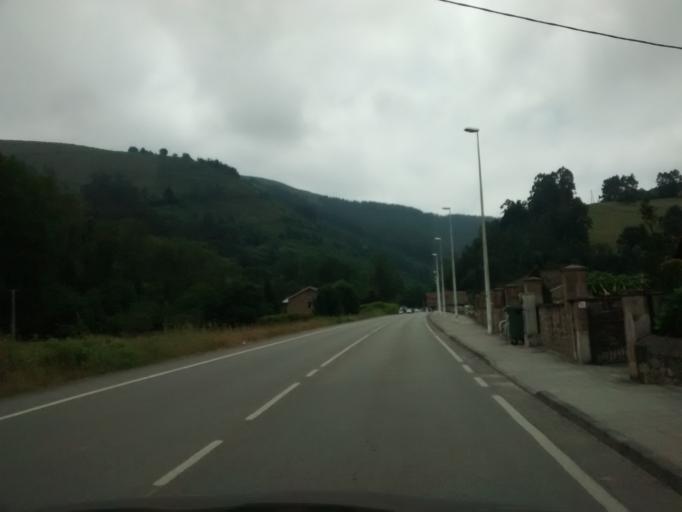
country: ES
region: Cantabria
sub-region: Provincia de Cantabria
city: Cabezon de la Sal
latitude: 43.2880
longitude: -4.2360
